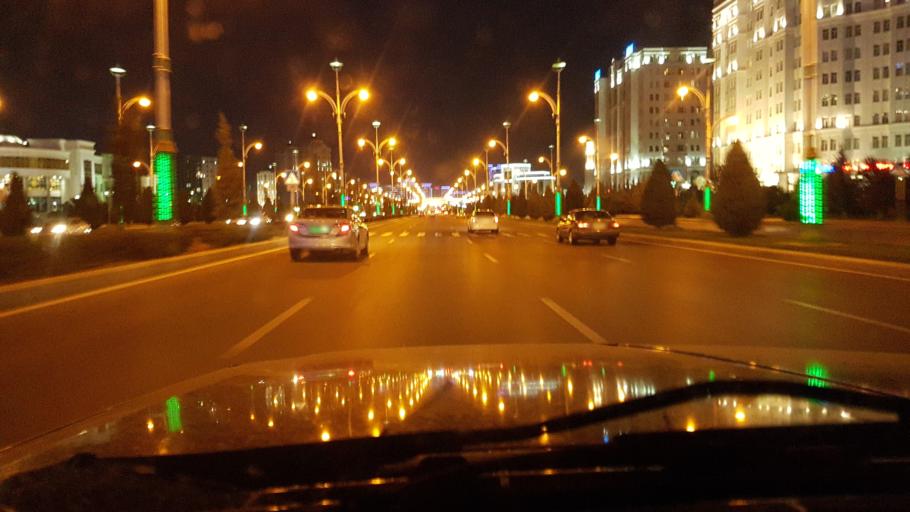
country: TM
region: Ahal
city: Ashgabat
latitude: 37.8996
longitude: 58.3529
